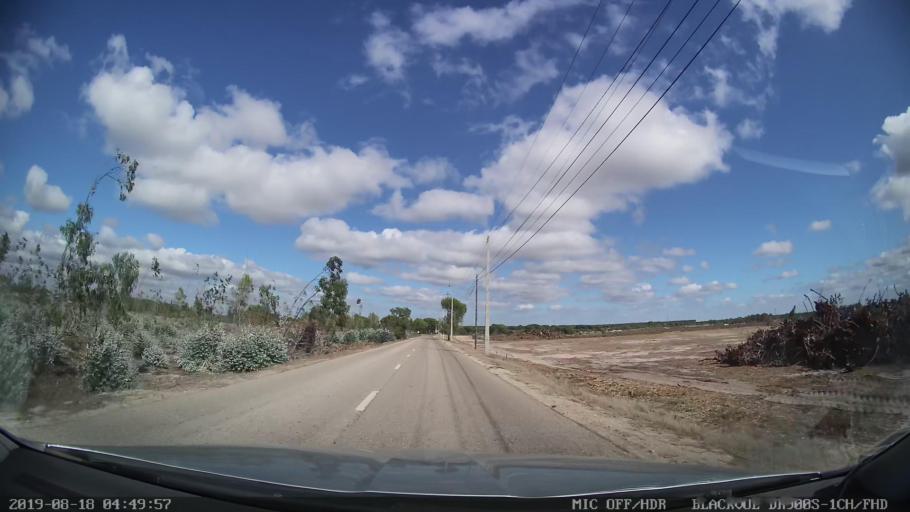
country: PT
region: Santarem
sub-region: Benavente
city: Benavente
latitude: 38.9375
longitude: -8.7876
